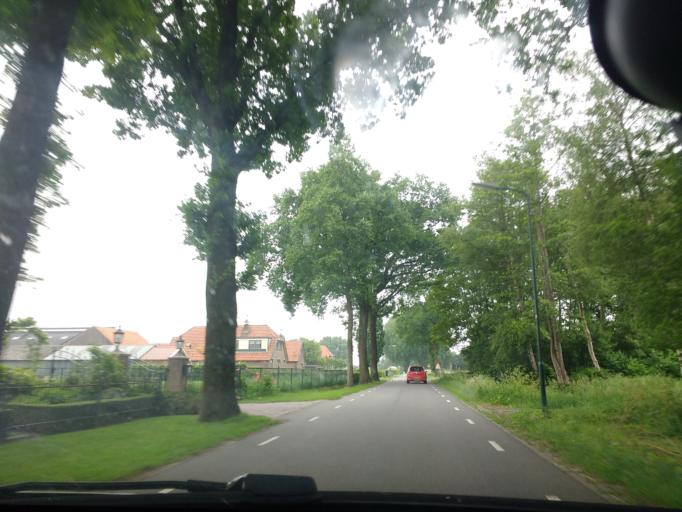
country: NL
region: Utrecht
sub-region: Gemeente Rhenen
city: Rhenen
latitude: 51.9834
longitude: 5.5952
